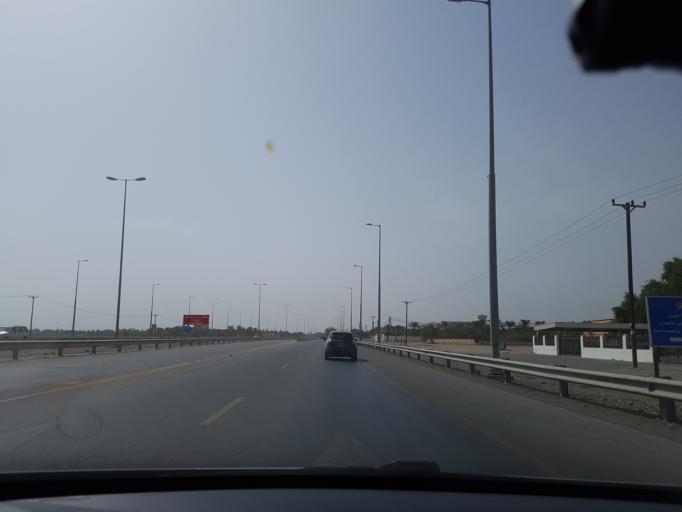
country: OM
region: Al Batinah
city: Al Khaburah
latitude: 23.9625
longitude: 57.0976
